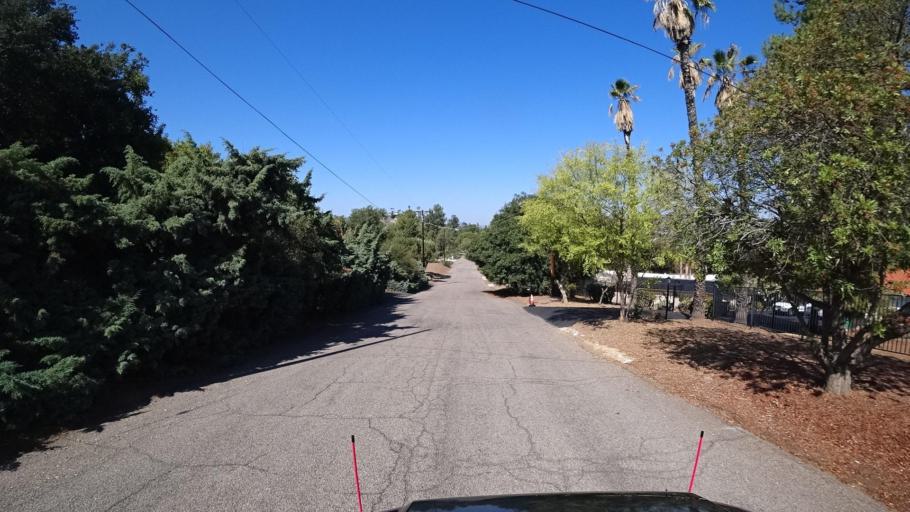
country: US
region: California
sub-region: San Diego County
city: Granite Hills
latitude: 32.7907
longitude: -116.9094
